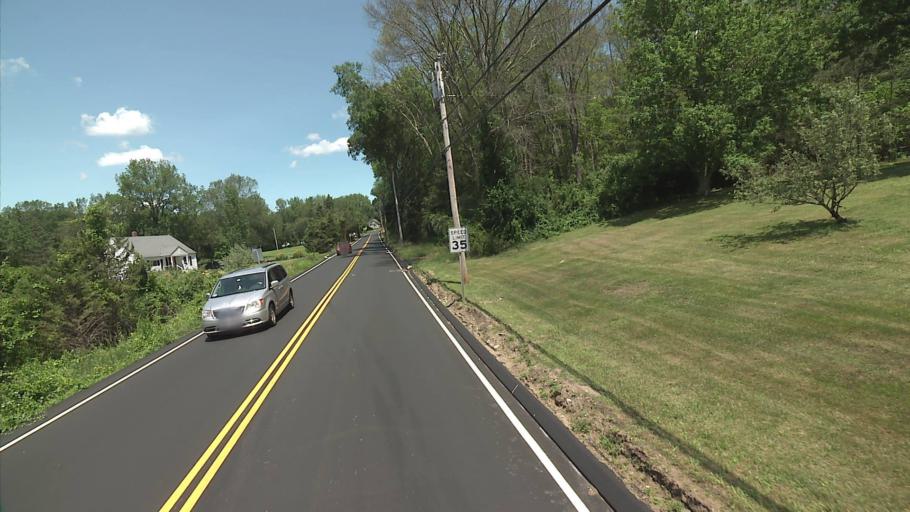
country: US
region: Connecticut
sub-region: New London County
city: Preston City
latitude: 41.5596
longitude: -71.8912
